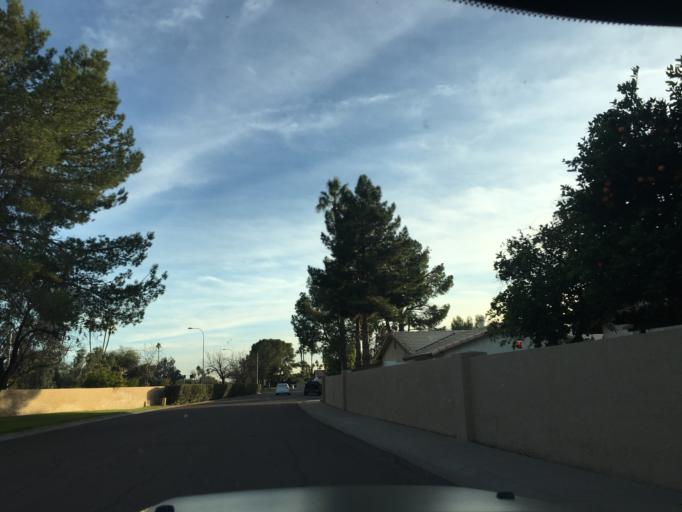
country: US
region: Arizona
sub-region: Maricopa County
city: Tempe
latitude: 33.3746
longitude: -111.9115
